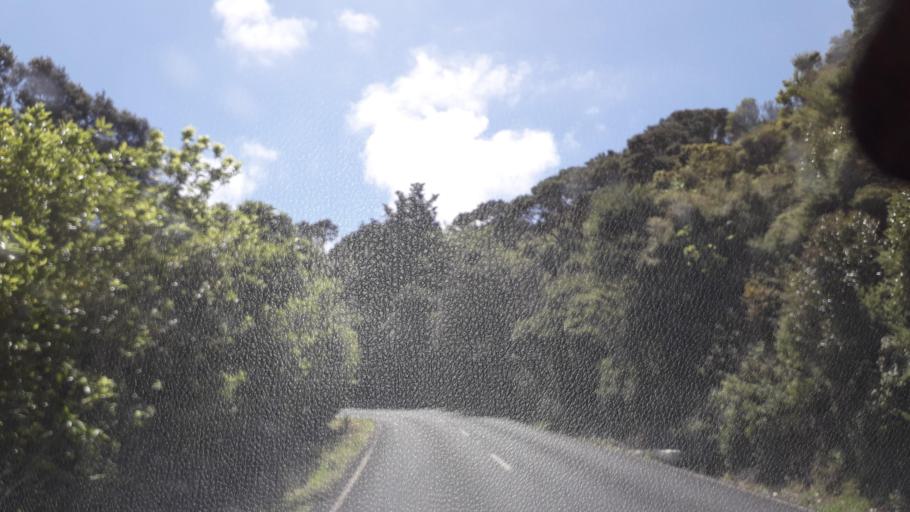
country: NZ
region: Northland
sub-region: Far North District
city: Paihia
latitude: -35.2553
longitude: 174.2645
